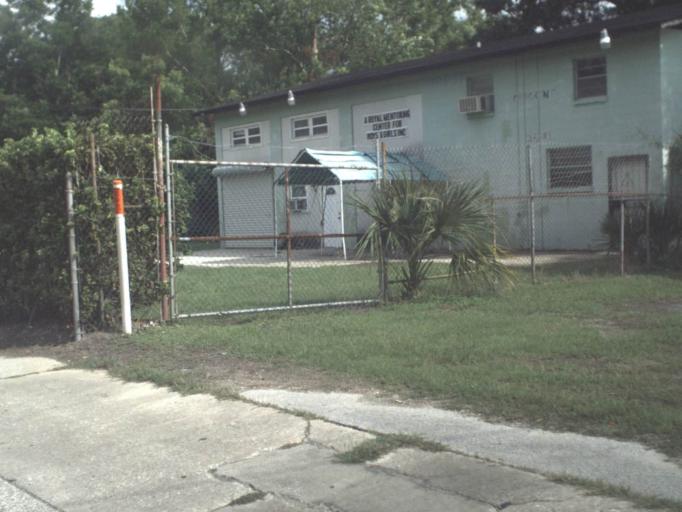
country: US
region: Florida
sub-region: Duval County
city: Jacksonville
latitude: 30.3525
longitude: -81.7056
